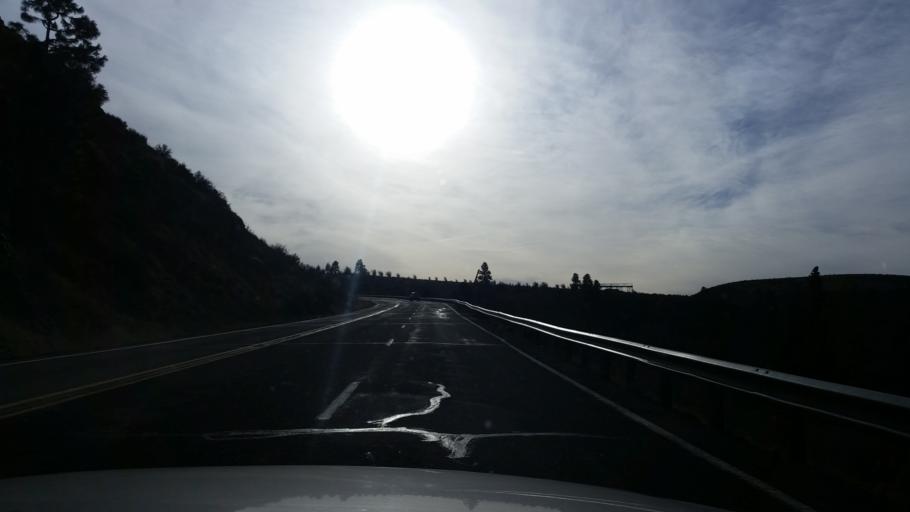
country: US
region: Washington
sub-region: Kittitas County
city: Ellensburg
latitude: 47.1224
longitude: -120.7251
